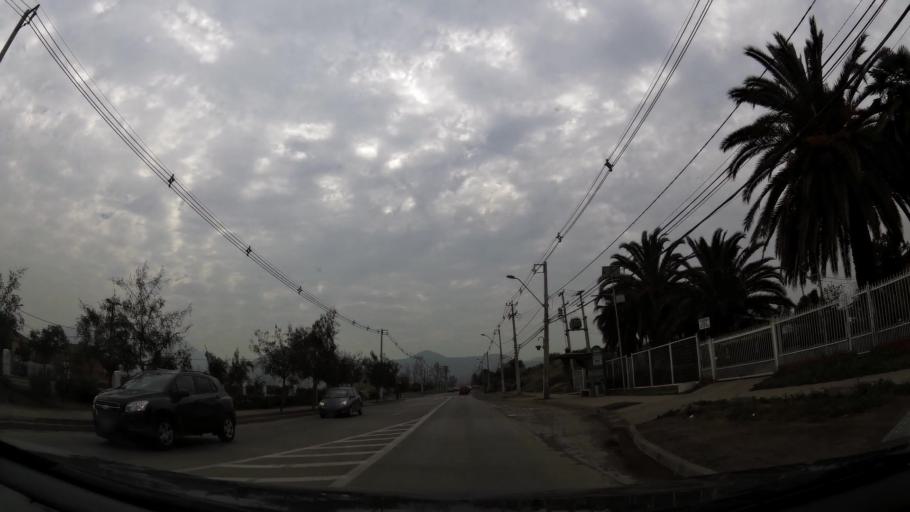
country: CL
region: Santiago Metropolitan
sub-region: Provincia de Chacabuco
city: Chicureo Abajo
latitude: -33.1930
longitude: -70.6775
